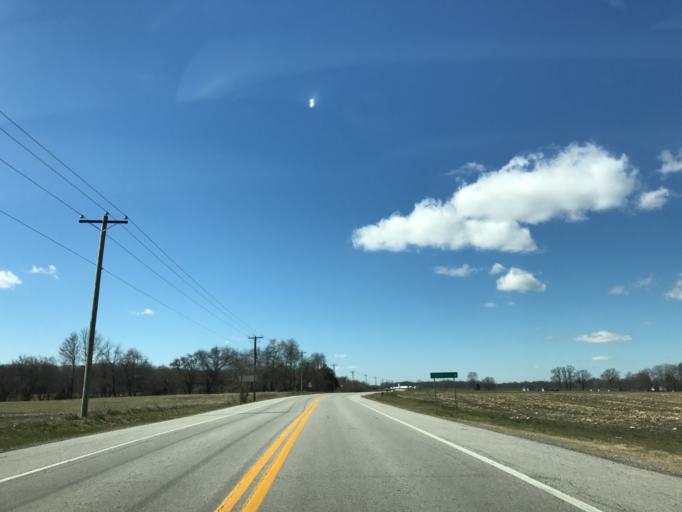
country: US
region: Maryland
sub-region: Queen Anne's County
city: Kingstown
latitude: 39.1232
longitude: -75.9434
